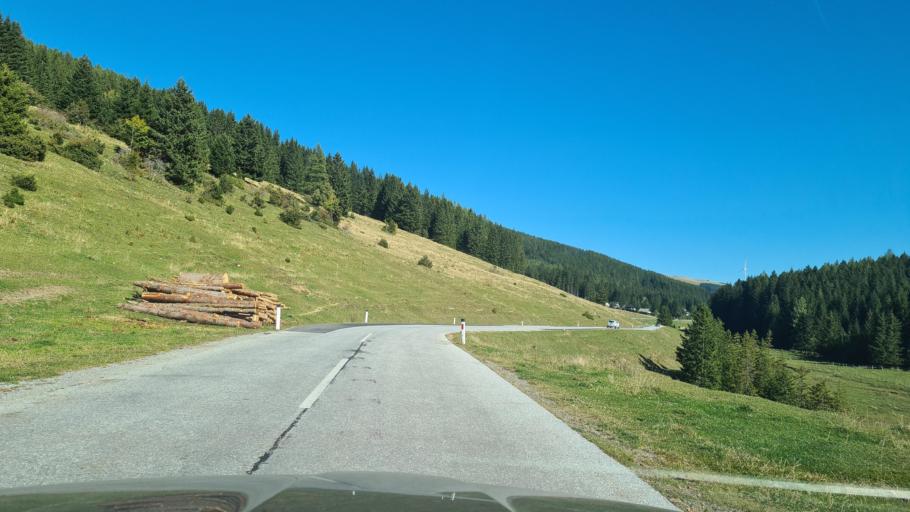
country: AT
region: Styria
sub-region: Politischer Bezirk Weiz
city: Passail
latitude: 47.3526
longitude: 15.4965
